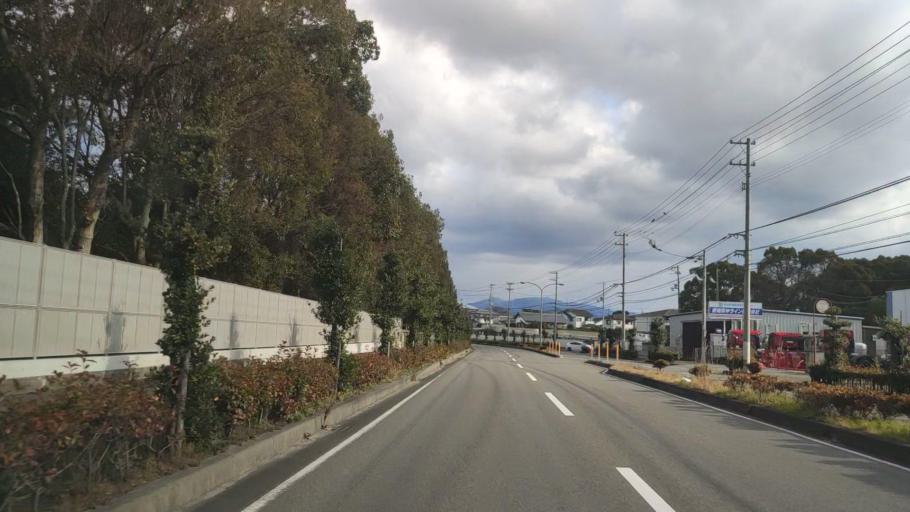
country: JP
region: Ehime
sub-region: Shikoku-chuo Shi
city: Matsuyama
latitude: 33.8471
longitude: 132.7118
